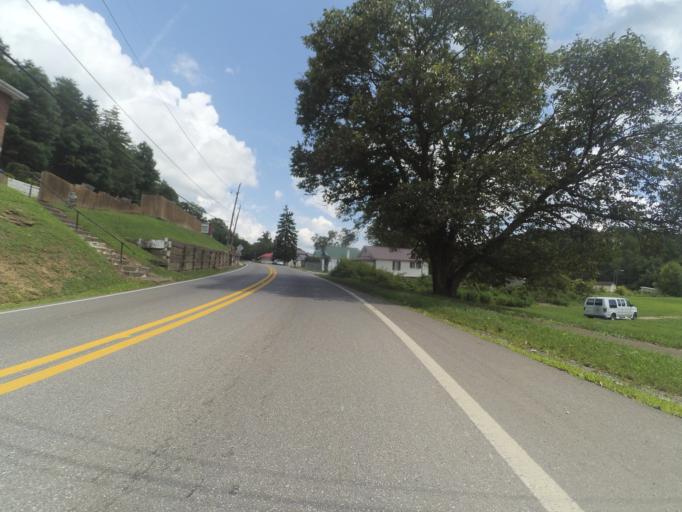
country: US
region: West Virginia
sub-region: Cabell County
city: Pea Ridge
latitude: 38.4117
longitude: -82.3601
